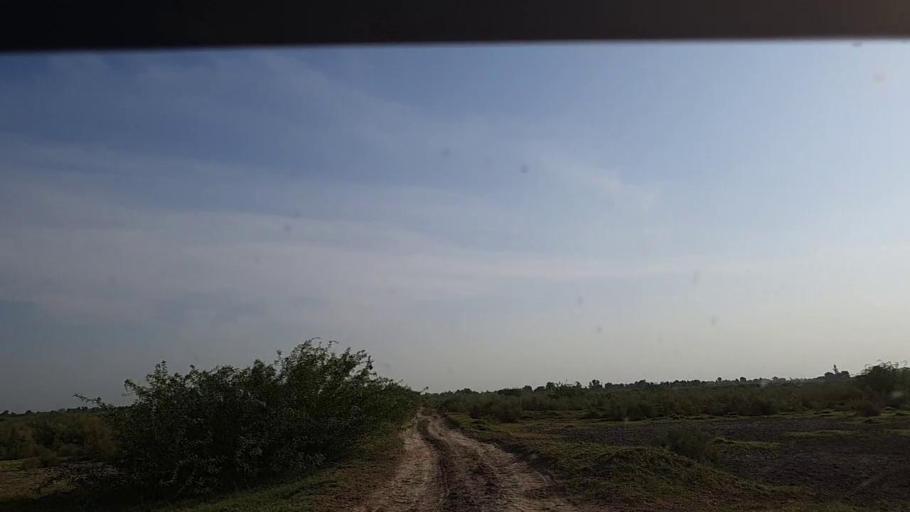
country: PK
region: Sindh
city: Pano Aqil
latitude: 27.9066
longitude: 69.2112
